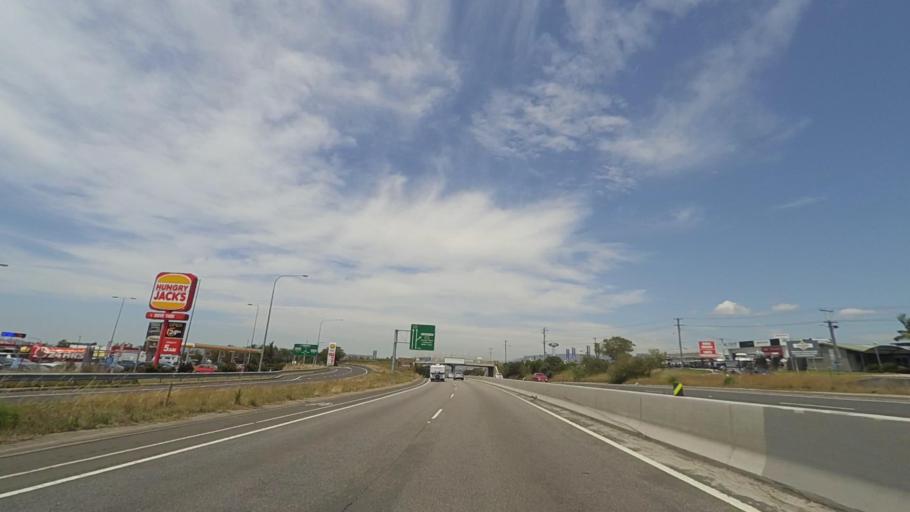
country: AU
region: New South Wales
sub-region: Shellharbour
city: Albion Park Rail
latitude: -34.5401
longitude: 150.7847
